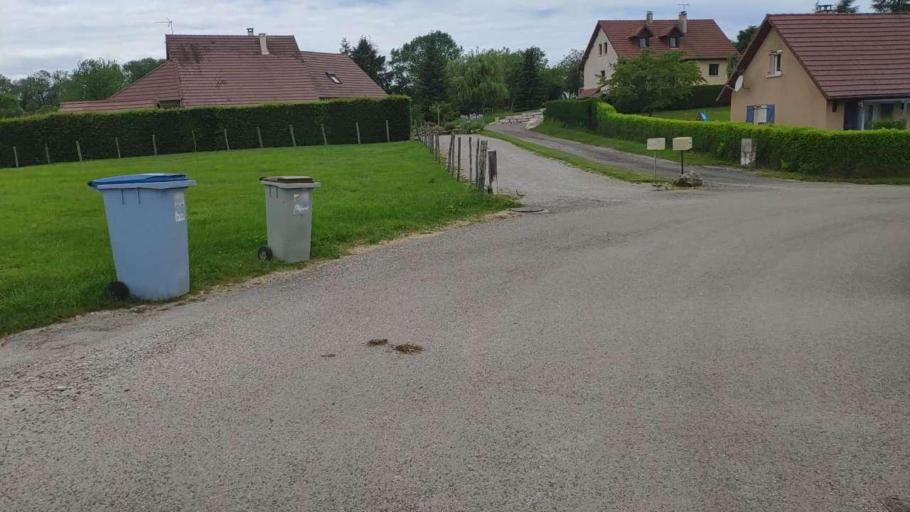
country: FR
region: Franche-Comte
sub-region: Departement du Jura
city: Lons-le-Saunier
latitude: 46.7514
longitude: 5.5625
